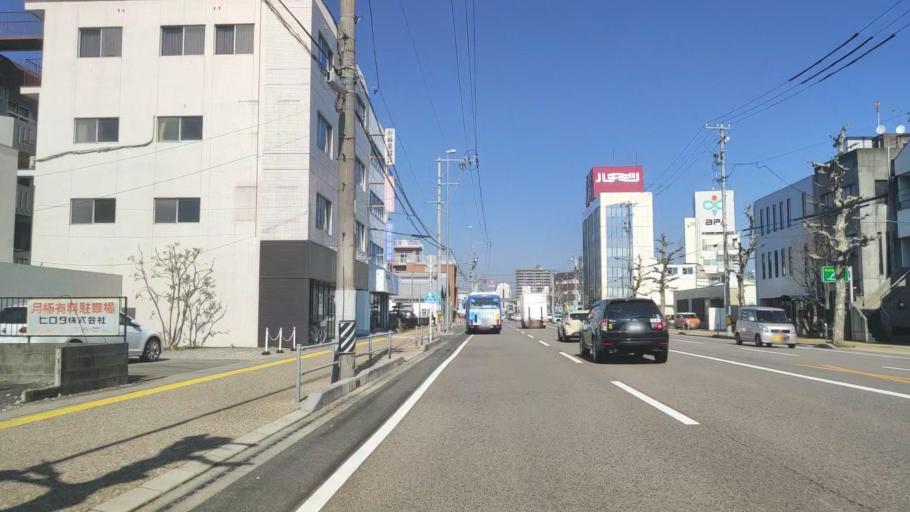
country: JP
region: Gifu
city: Gifu-shi
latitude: 35.4054
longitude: 136.7474
